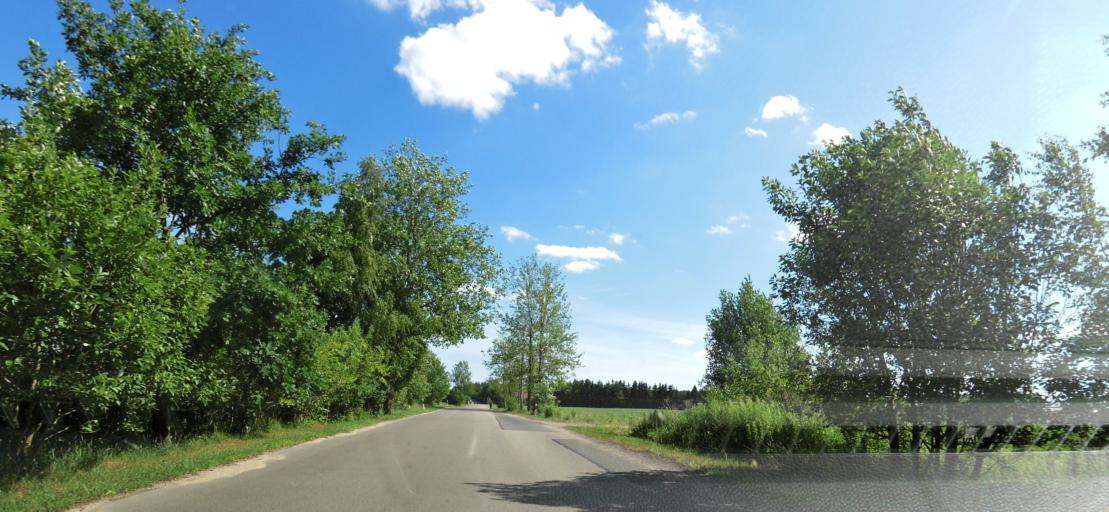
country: LT
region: Vilnius County
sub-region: Vilnius
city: Fabijoniskes
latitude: 54.8089
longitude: 25.3254
